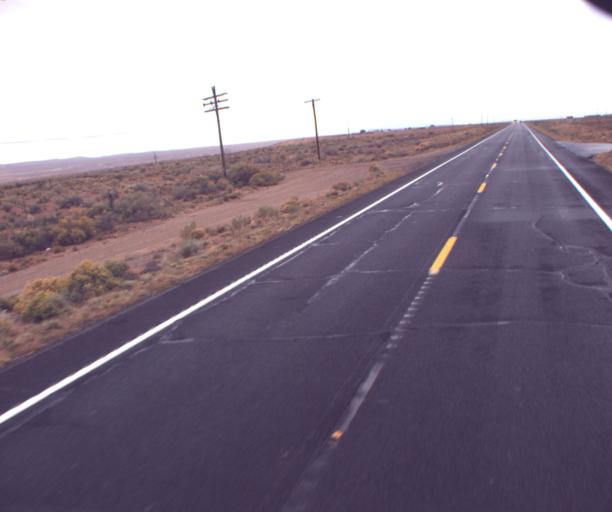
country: US
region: Arizona
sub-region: Coconino County
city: Tuba City
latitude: 36.1499
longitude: -111.1358
